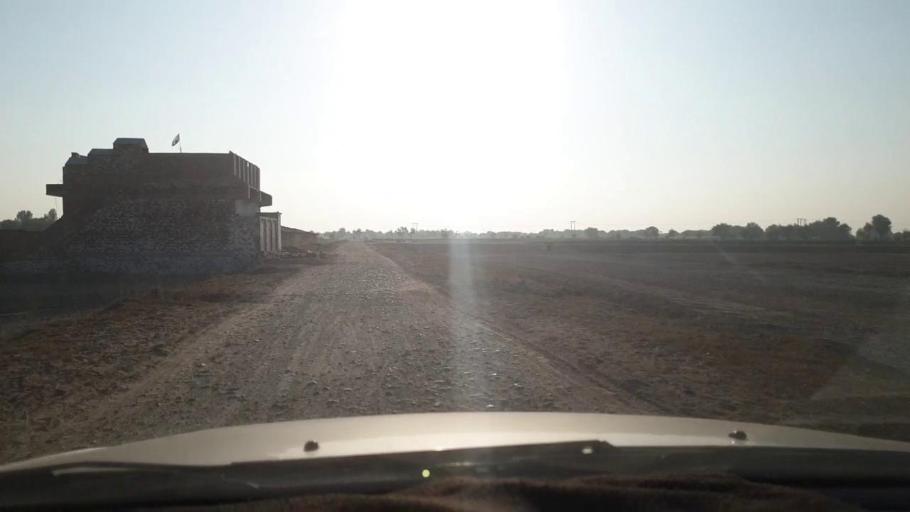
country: PK
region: Sindh
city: Mirpur Mathelo
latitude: 28.0037
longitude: 69.5293
